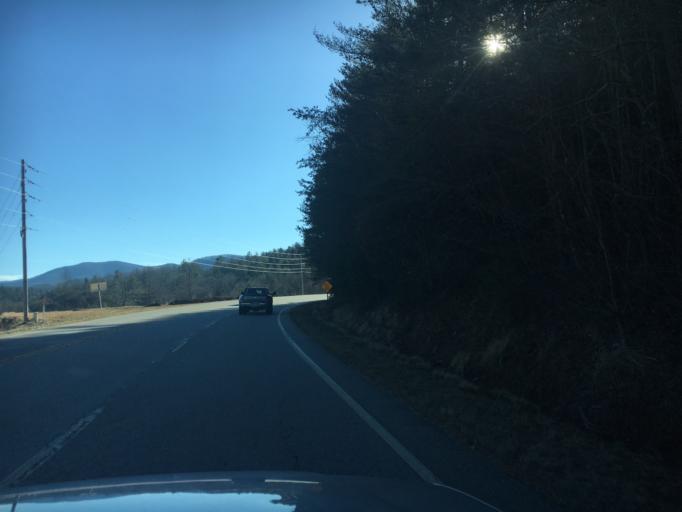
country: US
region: Georgia
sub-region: Union County
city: Blairsville
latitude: 34.7938
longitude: -83.8940
